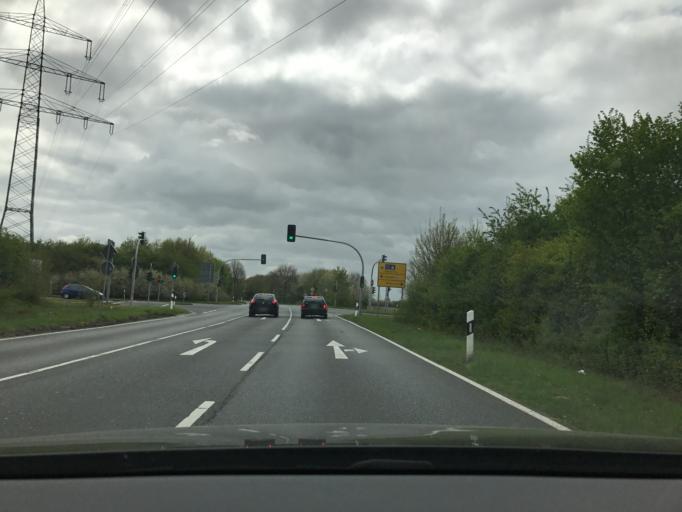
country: DE
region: North Rhine-Westphalia
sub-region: Regierungsbezirk Dusseldorf
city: Kaarst
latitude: 51.2679
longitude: 6.6048
